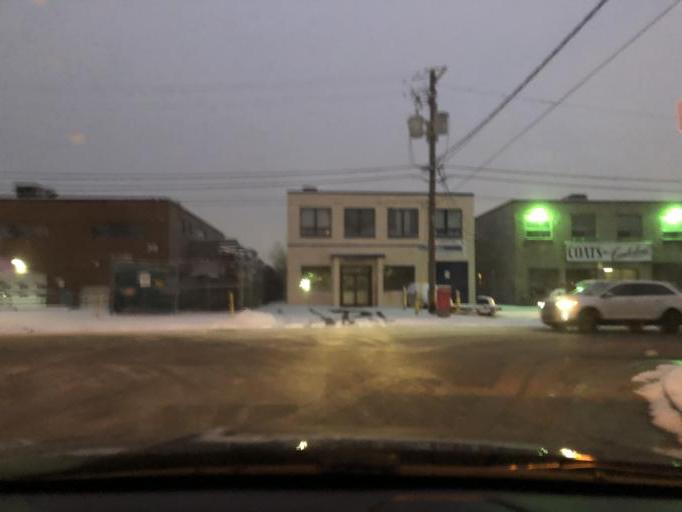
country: CA
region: Ontario
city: Toronto
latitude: 43.7046
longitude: -79.4729
